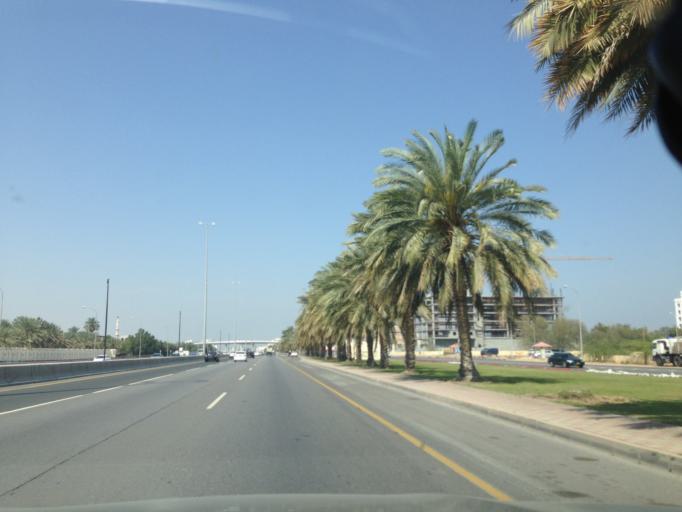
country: OM
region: Muhafazat Masqat
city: As Sib al Jadidah
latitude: 23.6194
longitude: 58.2413
